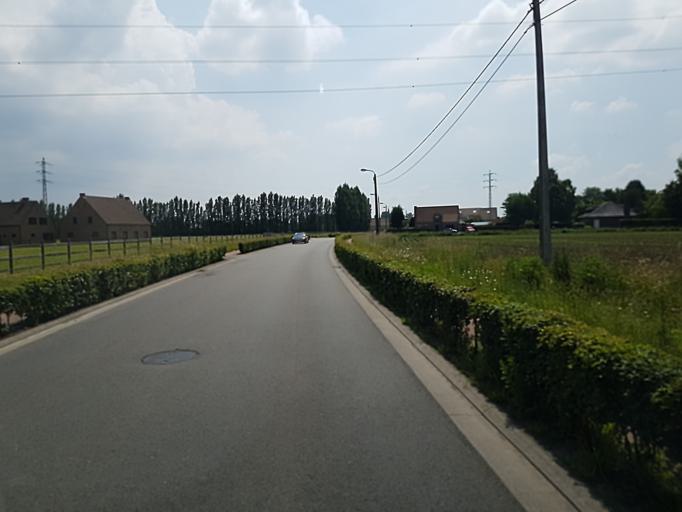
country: BE
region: Flanders
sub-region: Provincie Vlaams-Brabant
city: Londerzeel
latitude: 51.0258
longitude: 4.3180
